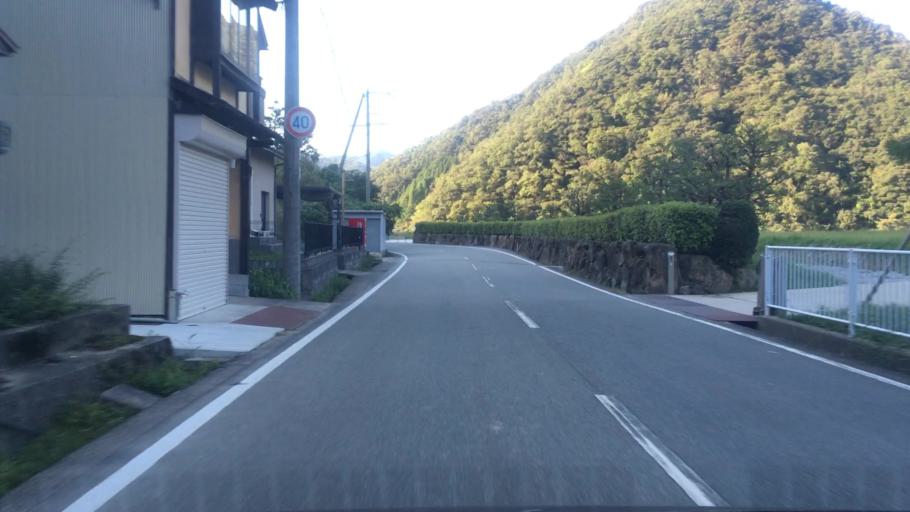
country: JP
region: Hyogo
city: Toyooka
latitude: 35.6153
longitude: 134.8266
